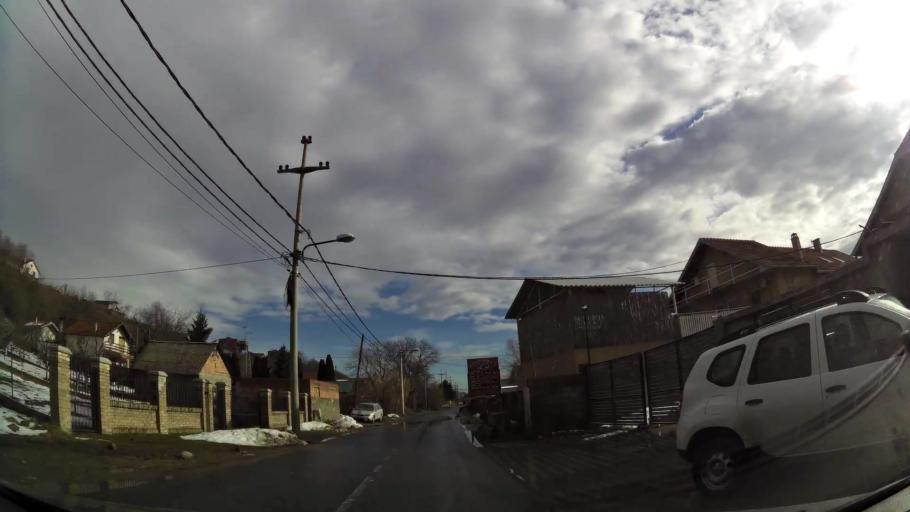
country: RS
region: Central Serbia
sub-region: Belgrade
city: Surcin
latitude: 44.7966
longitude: 20.3429
